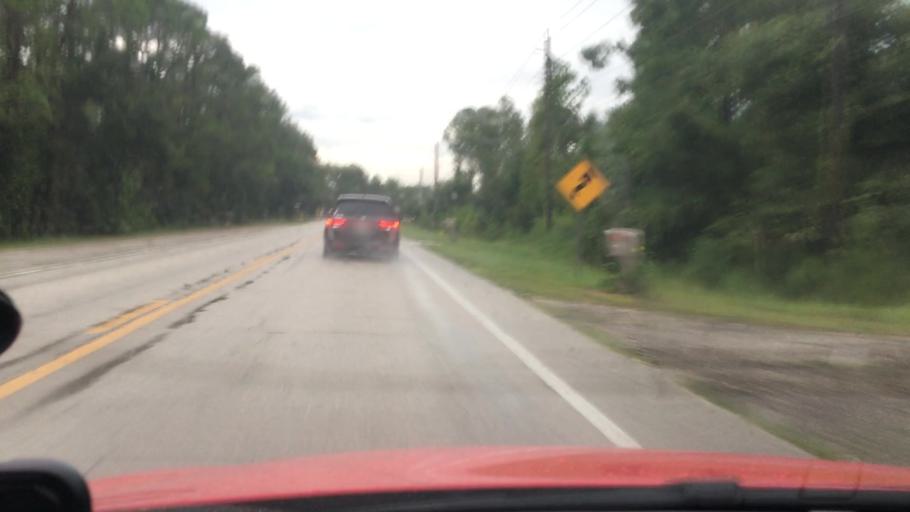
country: US
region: Florida
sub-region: Volusia County
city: Samsula-Spruce Creek
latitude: 29.0557
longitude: -81.0682
